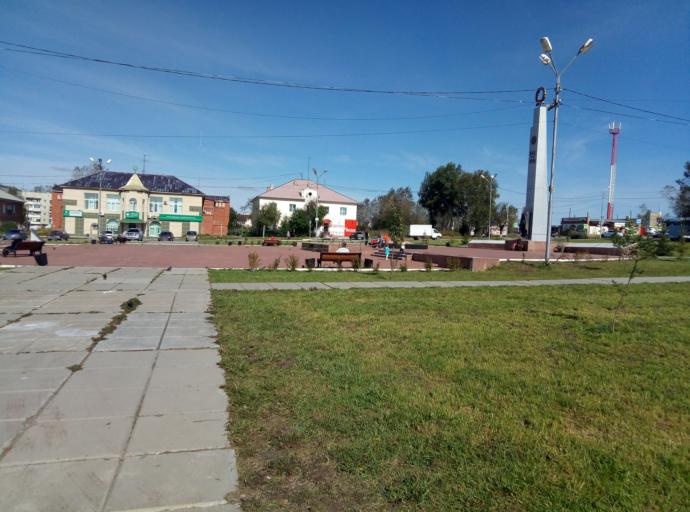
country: RU
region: Sverdlovsk
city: Karpinsk
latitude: 59.7746
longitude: 59.9931
